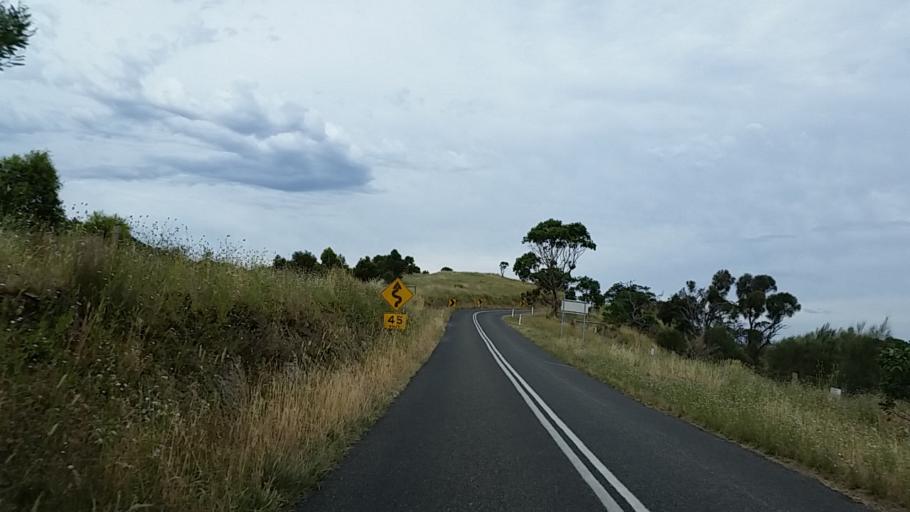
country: AU
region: South Australia
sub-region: Yankalilla
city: Normanville
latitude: -35.3991
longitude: 138.4189
